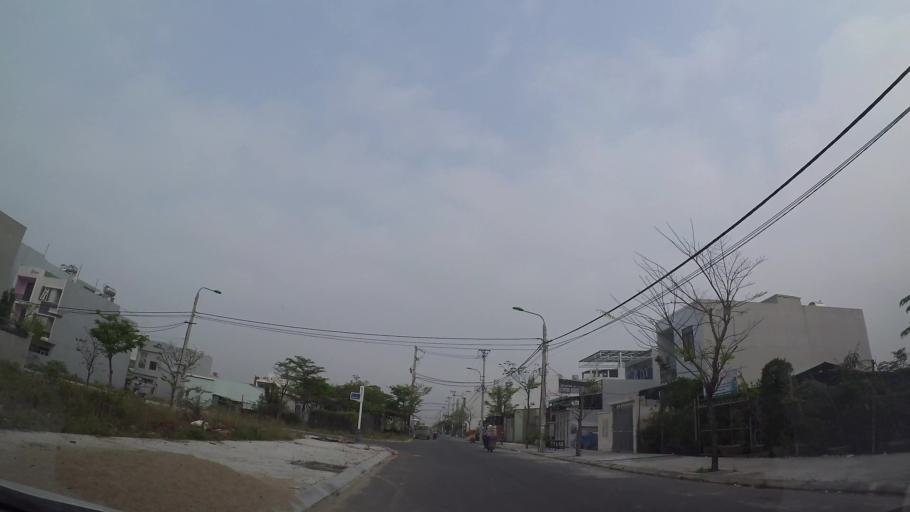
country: VN
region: Da Nang
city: Cam Le
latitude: 16.0133
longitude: 108.2230
